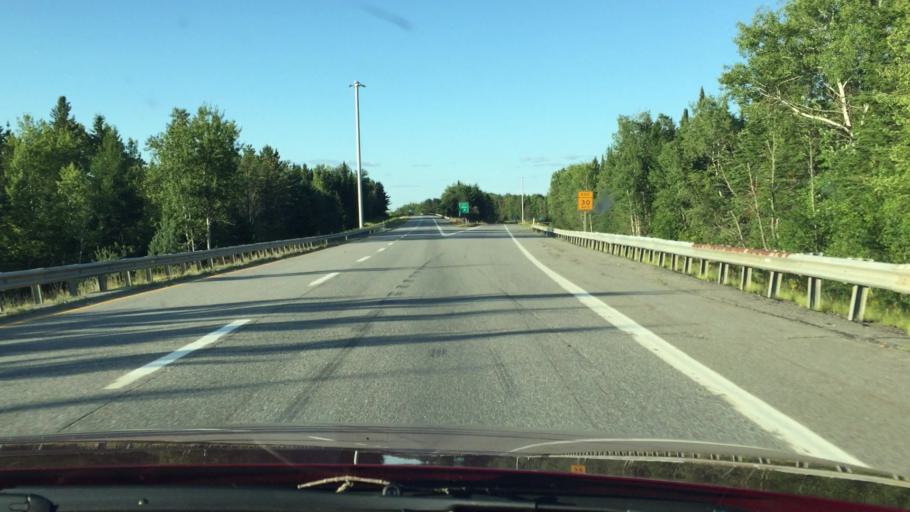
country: US
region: Maine
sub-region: Penobscot County
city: Patten
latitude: 45.8684
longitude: -68.4152
